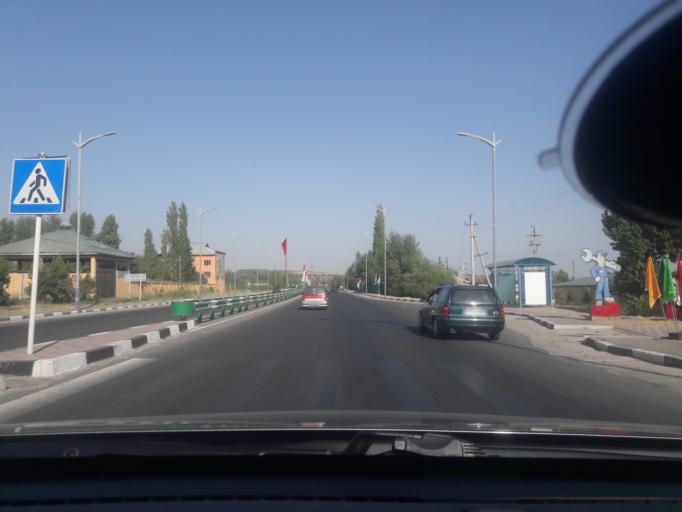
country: TJ
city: Shahrinav
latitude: 38.5754
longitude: 68.3506
